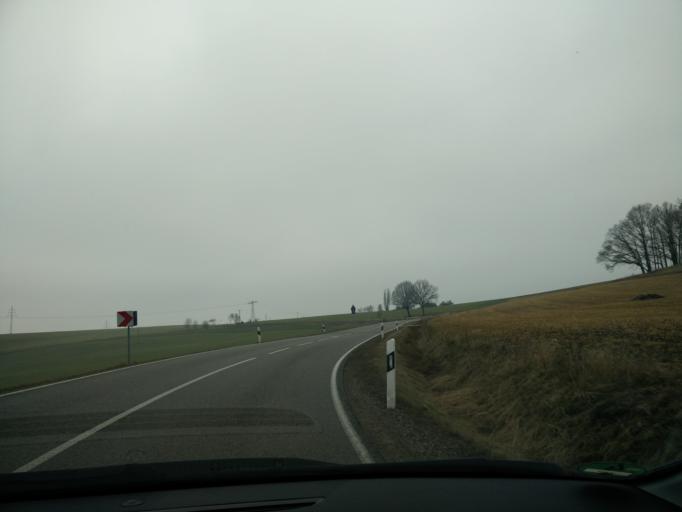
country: DE
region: Saxony
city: Wechselburg
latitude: 51.0048
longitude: 12.7518
